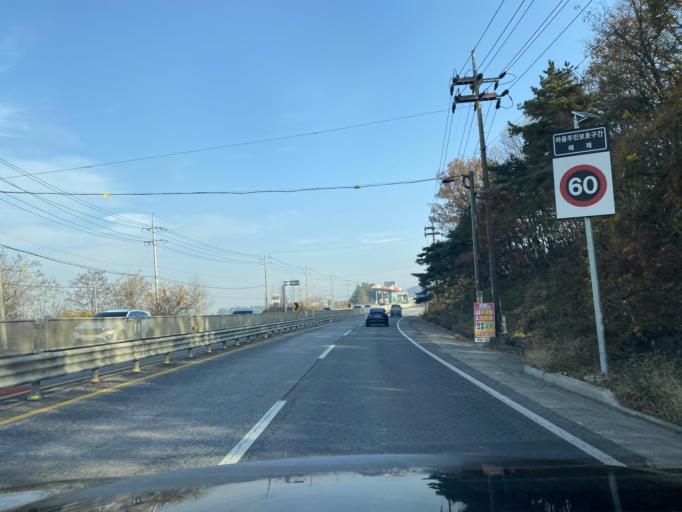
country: KR
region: Chungcheongnam-do
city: Yesan
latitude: 36.7430
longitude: 126.8607
